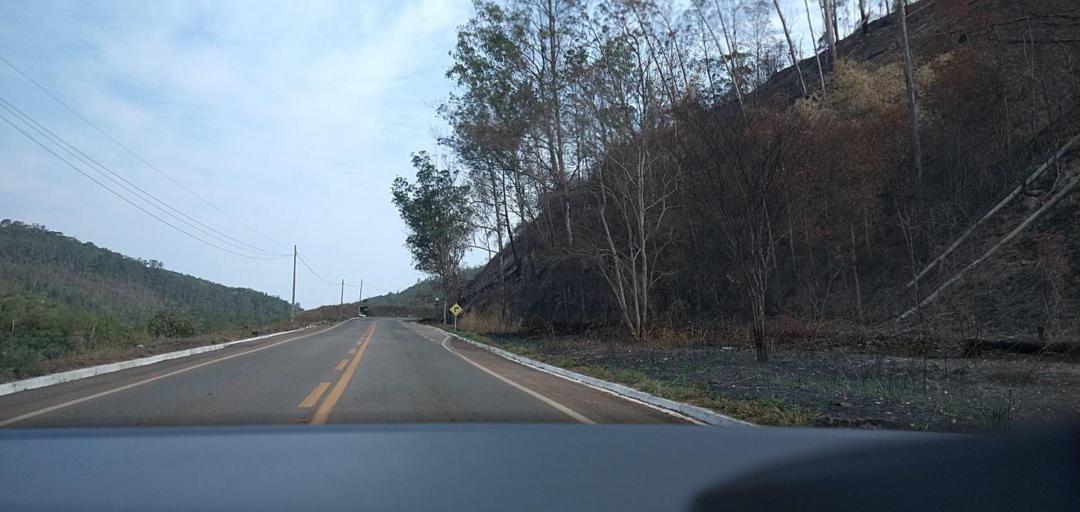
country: BR
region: Minas Gerais
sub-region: Rio Piracicaba
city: Rio Piracicaba
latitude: -19.8730
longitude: -43.1218
